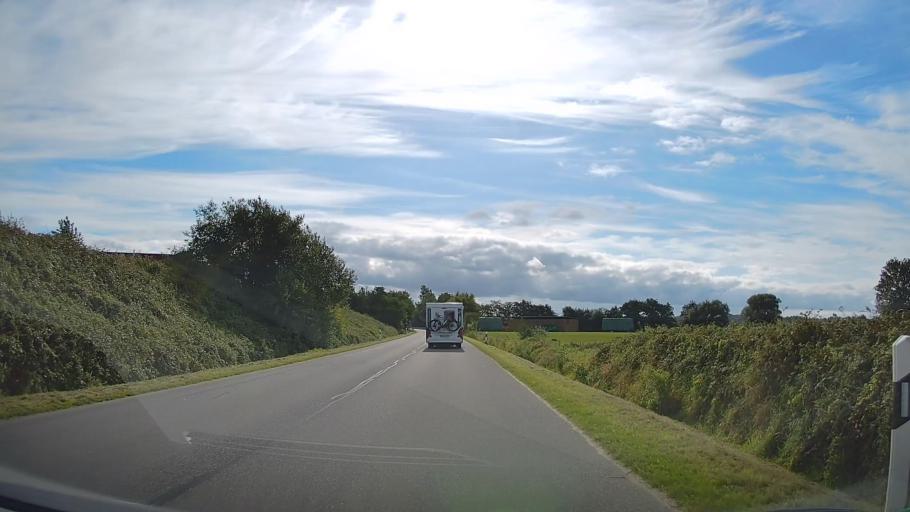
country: DE
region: Schleswig-Holstein
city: Glucksburg
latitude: 54.8620
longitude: 9.5900
